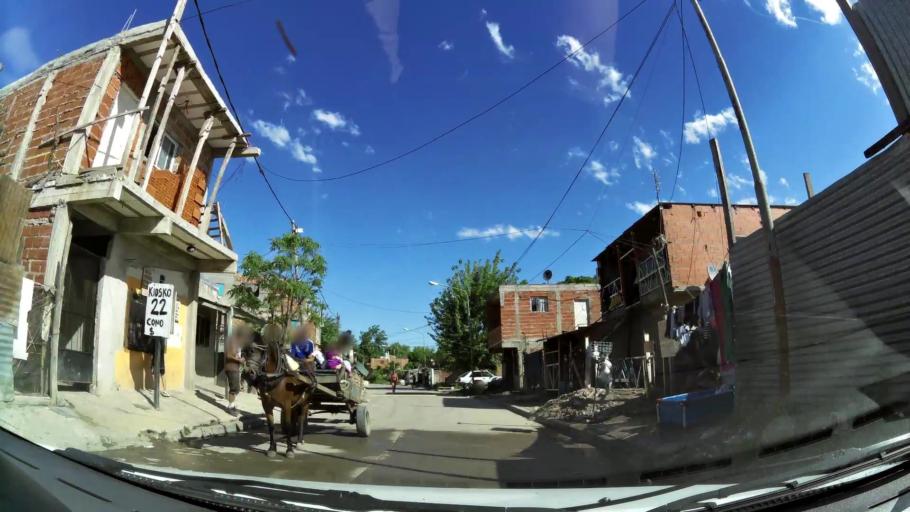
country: AR
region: Buenos Aires
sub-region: Partido de General San Martin
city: General San Martin
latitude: -34.5202
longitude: -58.5852
